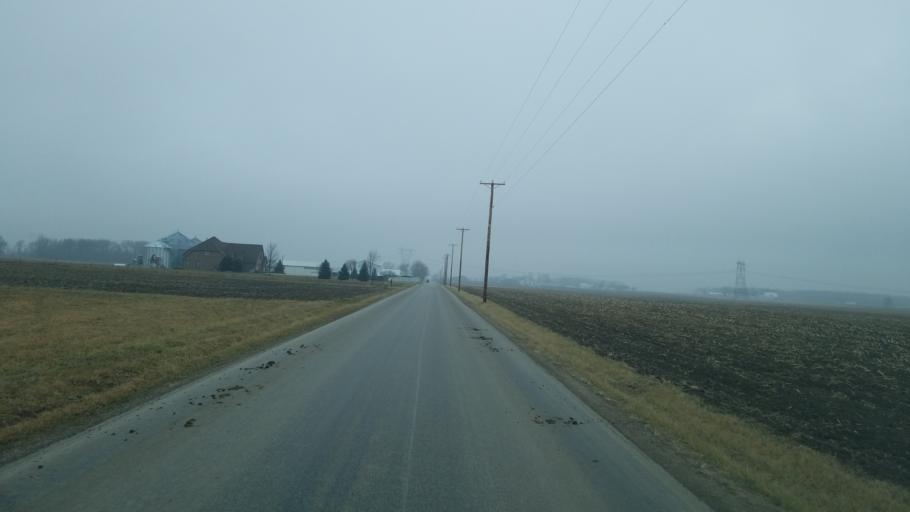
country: US
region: Indiana
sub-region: Adams County
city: Berne
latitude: 40.7034
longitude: -84.9753
